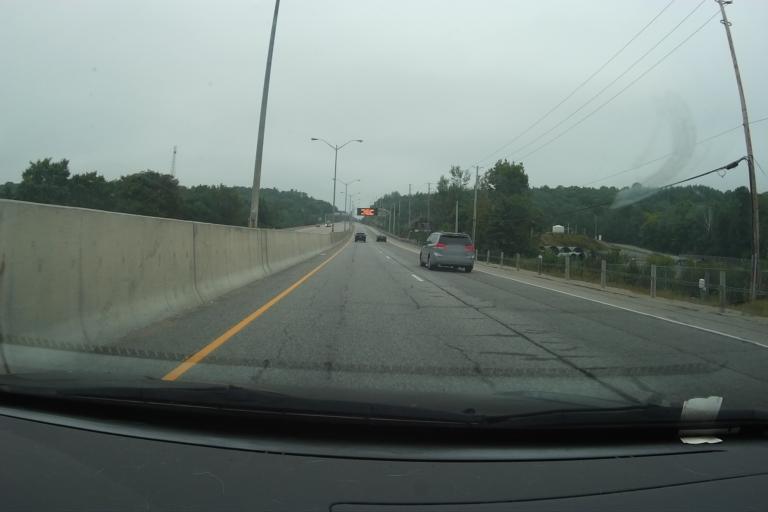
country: CA
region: Ontario
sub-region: Nipissing District
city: North Bay
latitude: 46.3367
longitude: -79.4670
